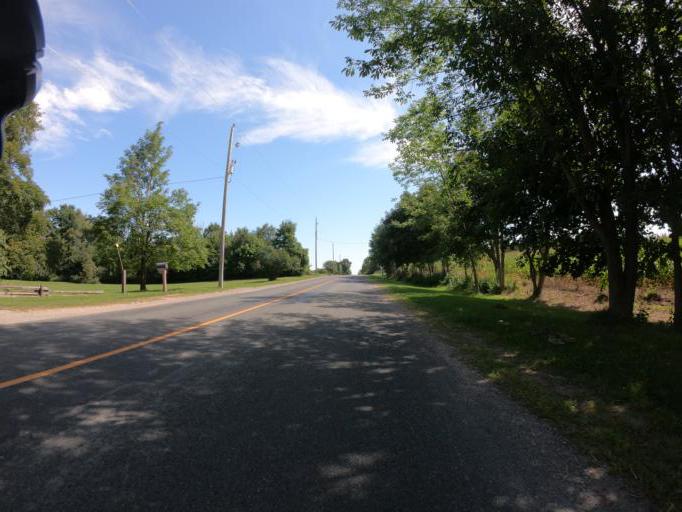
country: CA
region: Ontario
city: Waterloo
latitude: 43.4946
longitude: -80.4352
